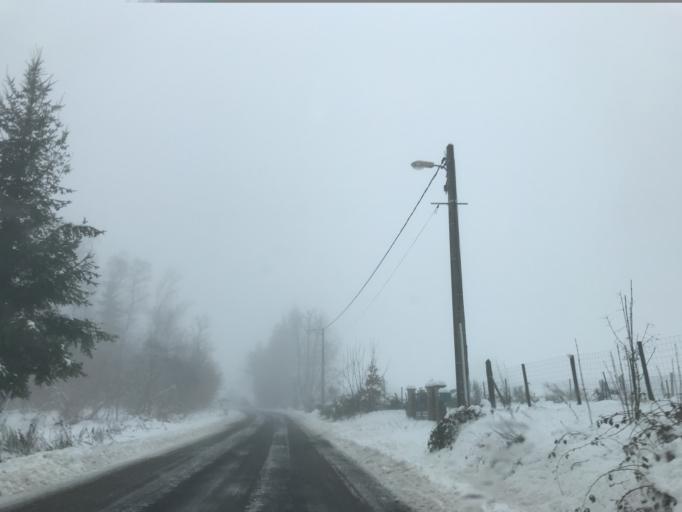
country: FR
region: Auvergne
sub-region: Departement du Puy-de-Dome
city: Job
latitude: 45.7156
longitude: 3.7122
